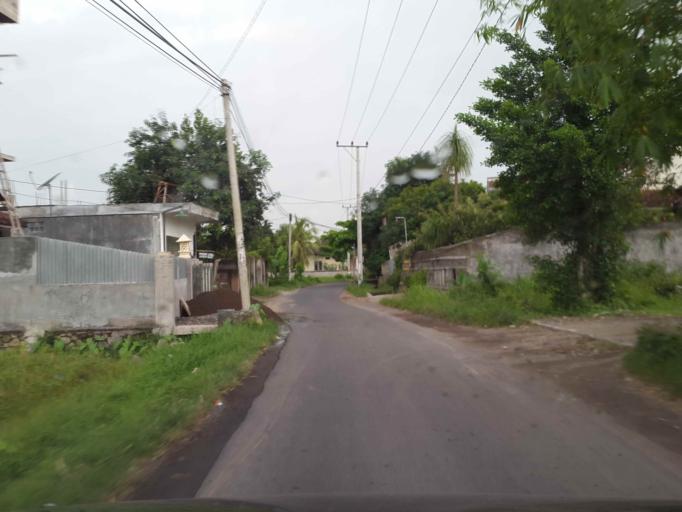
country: ID
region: West Nusa Tenggara
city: Kekeri
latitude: -8.5558
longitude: 116.1155
